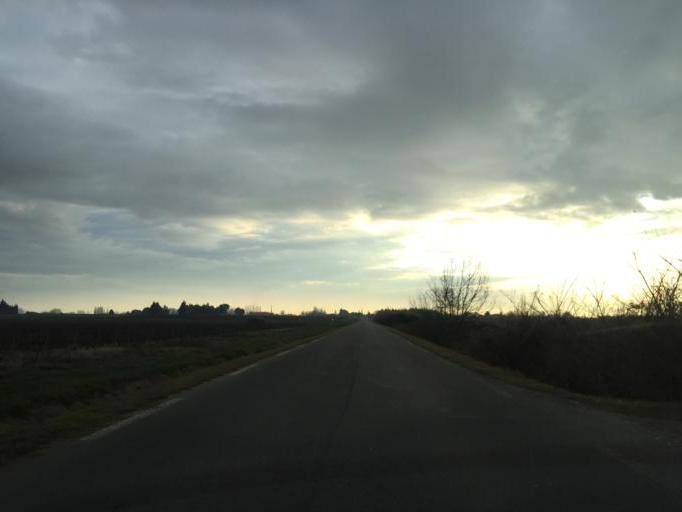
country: FR
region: Provence-Alpes-Cote d'Azur
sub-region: Departement du Vaucluse
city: Jonquieres
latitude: 44.1267
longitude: 4.8664
